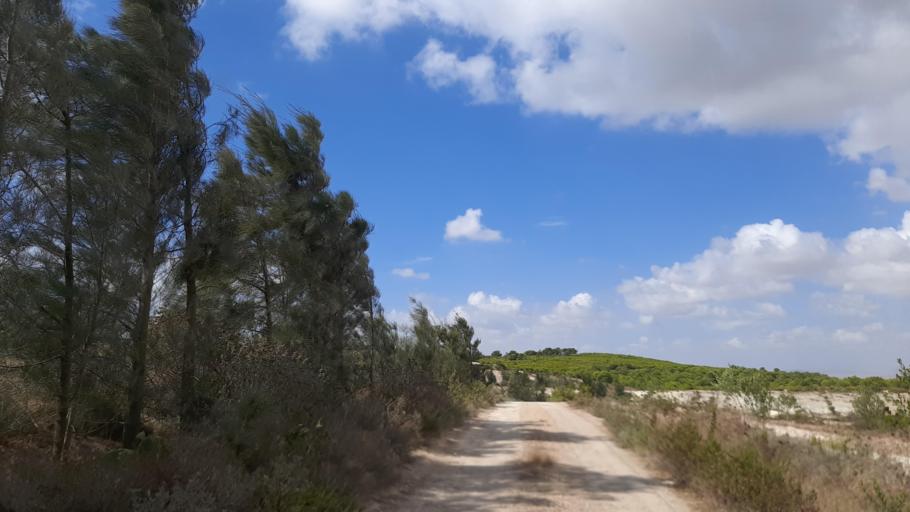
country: TN
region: Zaghwan
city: Zaghouan
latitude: 36.4980
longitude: 10.1740
